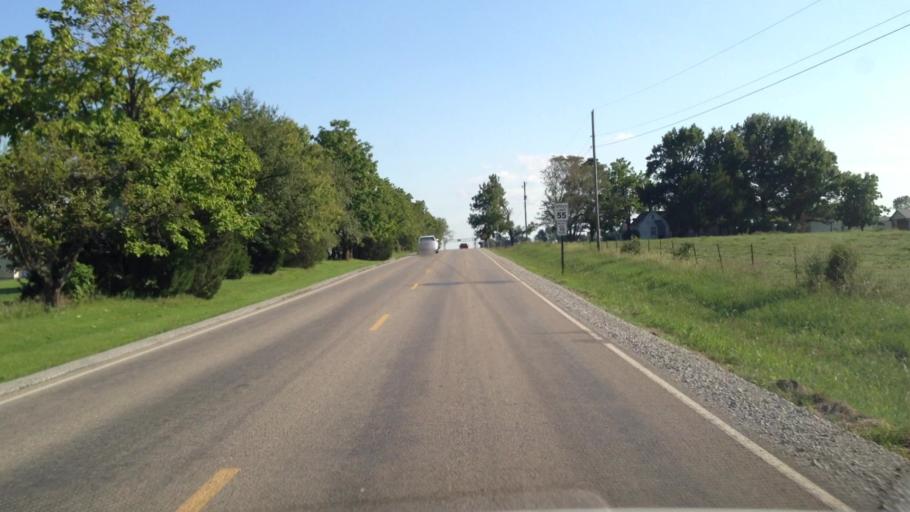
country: US
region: Kansas
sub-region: Crawford County
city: Pittsburg
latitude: 37.3672
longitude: -94.6315
